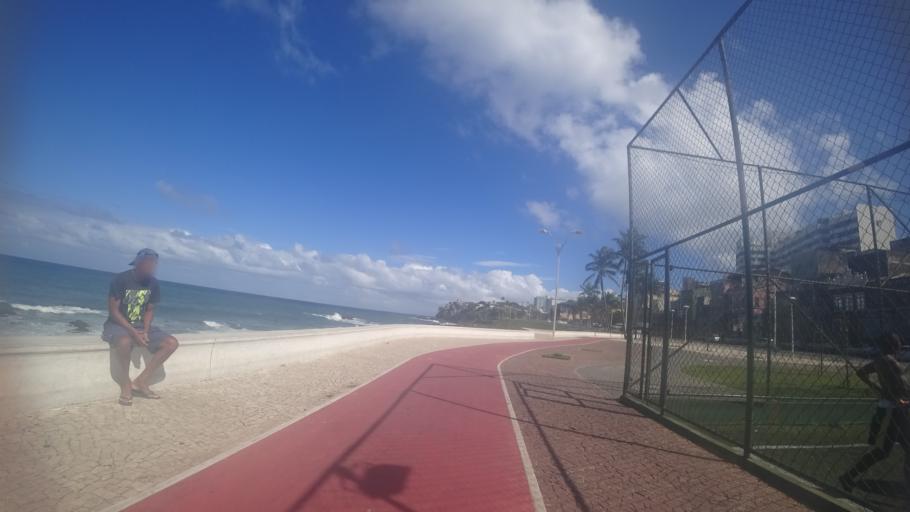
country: BR
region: Bahia
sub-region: Salvador
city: Salvador
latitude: -13.0114
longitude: -38.4936
